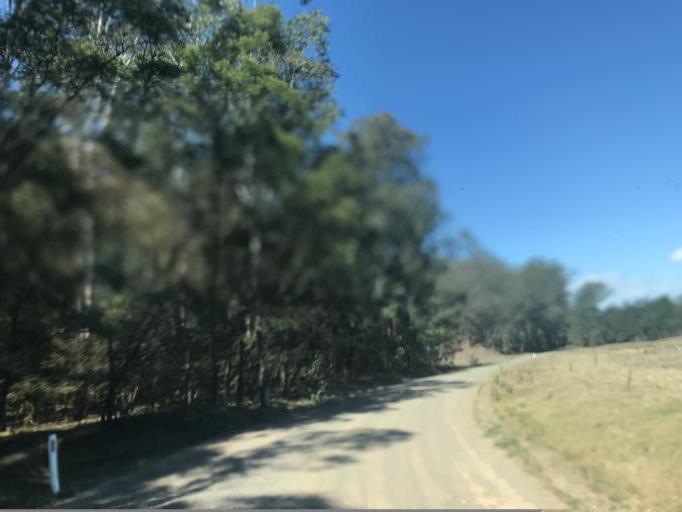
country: AU
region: New South Wales
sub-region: Hornsby Shire
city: Glenorie
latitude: -33.2191
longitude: 150.9799
